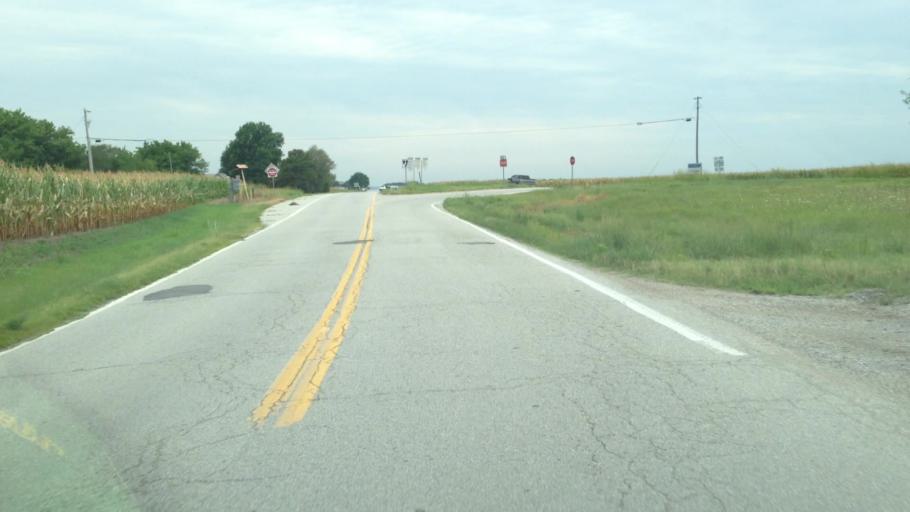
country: US
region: Oklahoma
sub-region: Delaware County
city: Cleora
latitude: 36.6271
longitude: -94.9824
